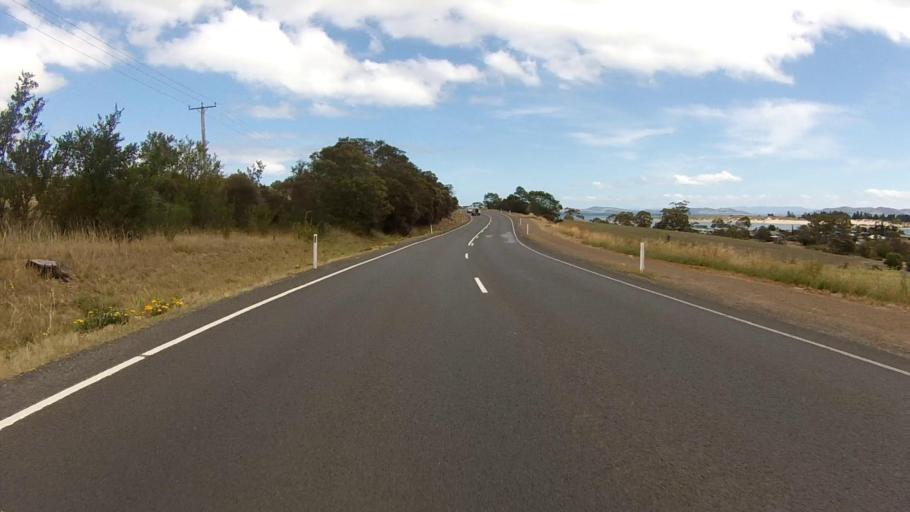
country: AU
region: Tasmania
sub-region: Sorell
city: Sorell
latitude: -42.8364
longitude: 147.6238
